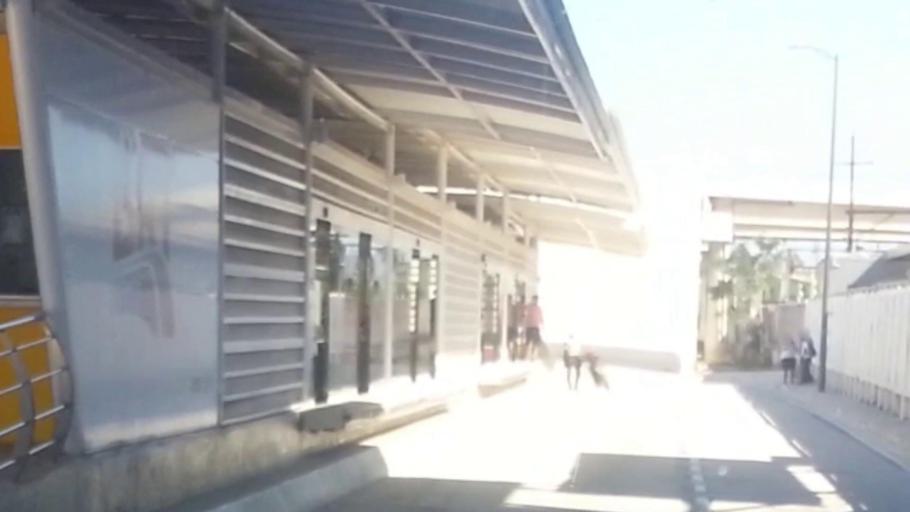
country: BR
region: Rio de Janeiro
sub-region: Nilopolis
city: Nilopolis
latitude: -22.8656
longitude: -43.4082
